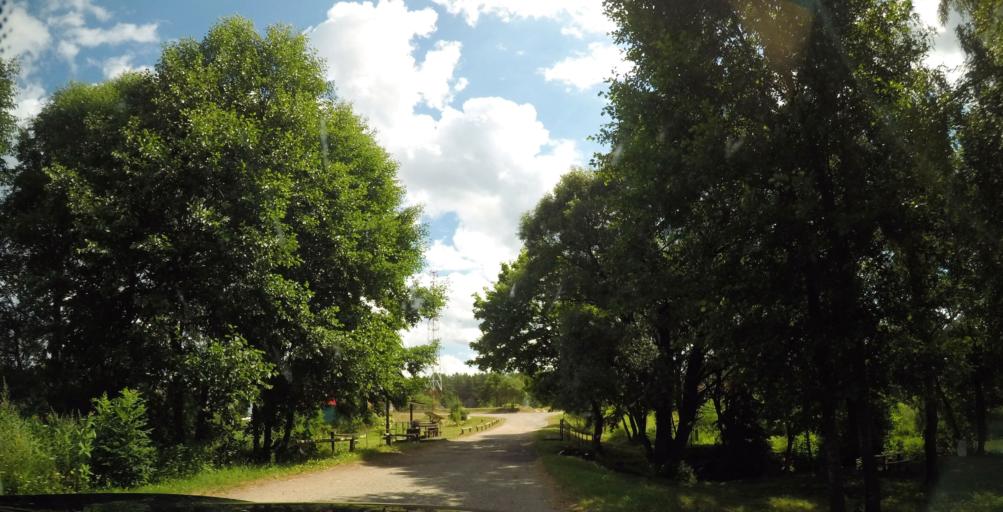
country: BY
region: Grodnenskaya
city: Skidal'
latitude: 53.8209
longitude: 24.2453
